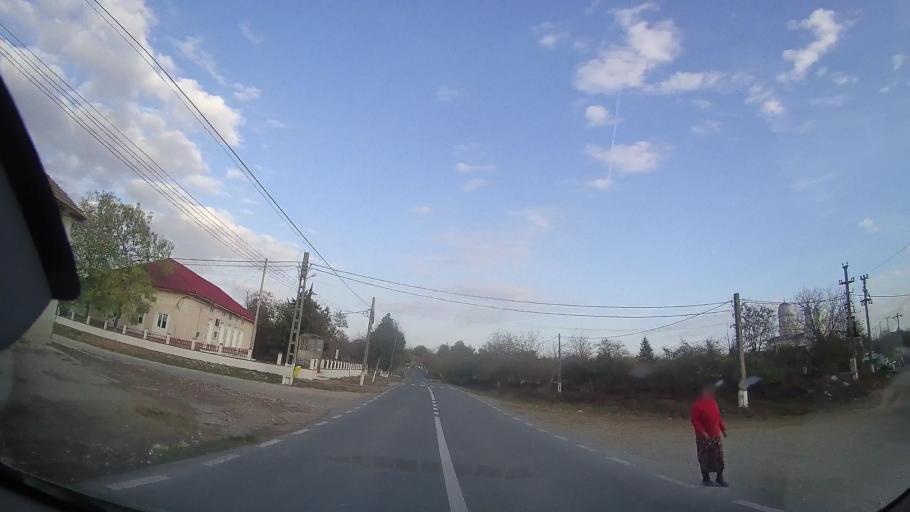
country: RO
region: Constanta
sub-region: Comuna Independenta
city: Independenta
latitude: 43.9620
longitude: 28.1394
